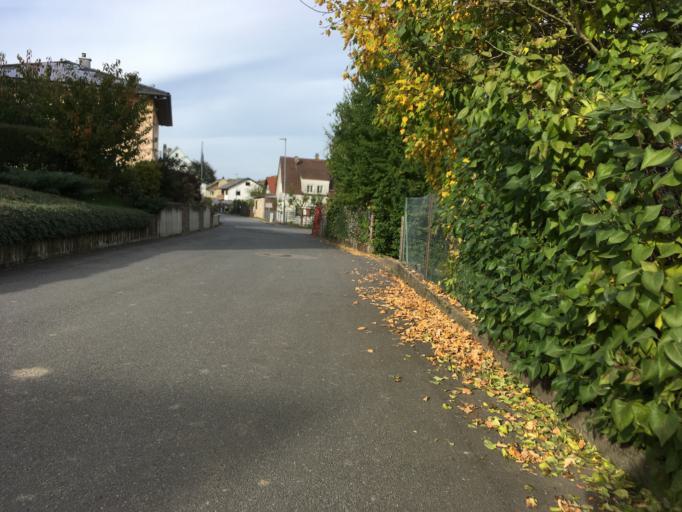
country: DE
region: Baden-Wuerttemberg
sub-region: Karlsruhe Region
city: Rosenberg
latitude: 49.5185
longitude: 9.4403
